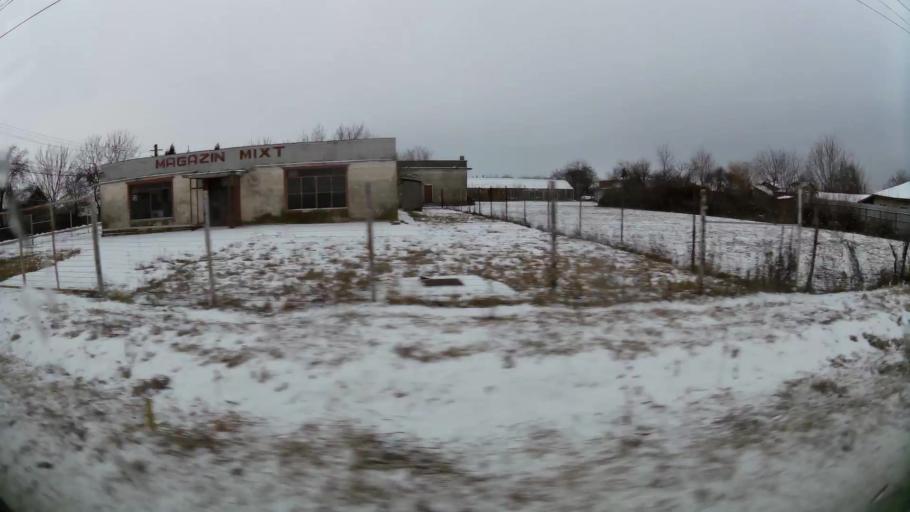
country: RO
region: Prahova
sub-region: Comuna Berceni
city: Corlatesti
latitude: 44.9253
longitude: 26.0712
